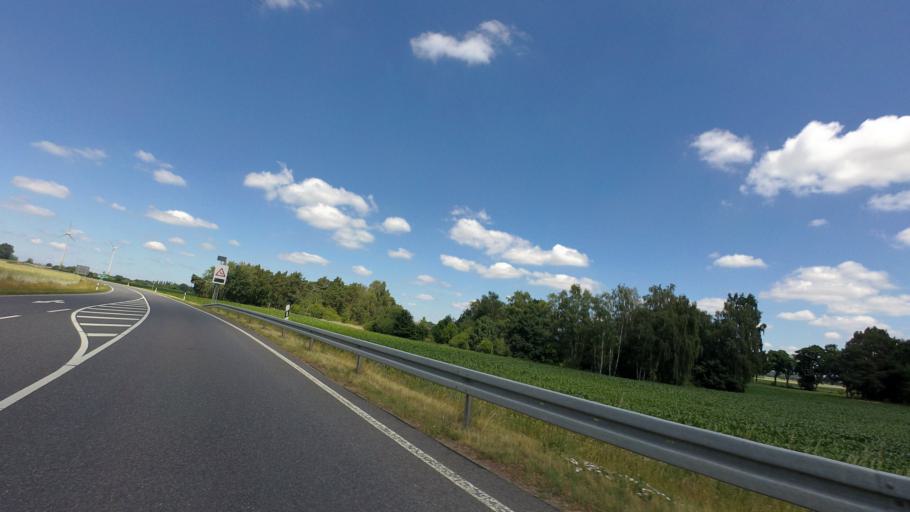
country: DE
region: Brandenburg
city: Luckau
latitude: 51.8314
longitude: 13.6851
